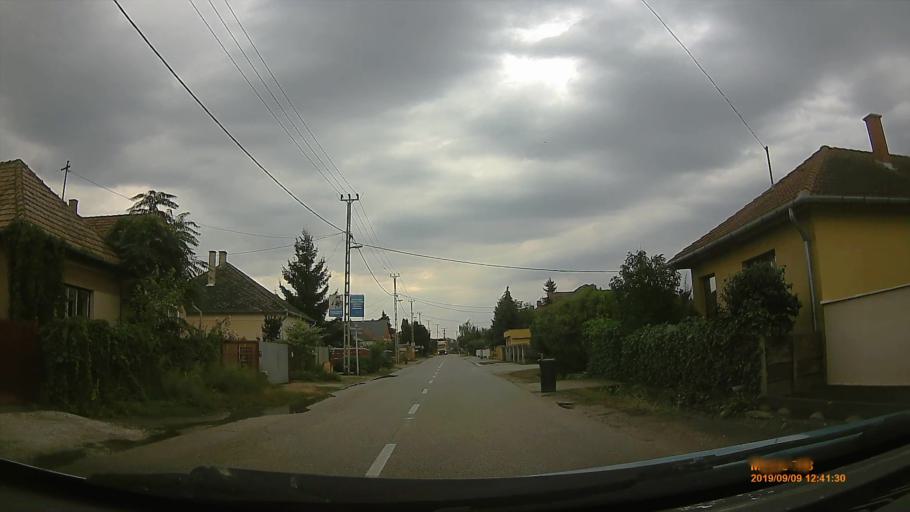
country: HU
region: Szabolcs-Szatmar-Bereg
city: Nyirpazony
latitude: 47.9795
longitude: 21.8016
